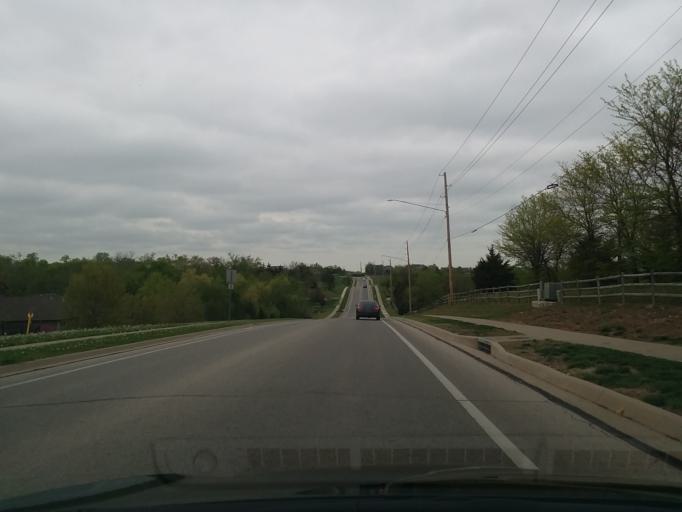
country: US
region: Kansas
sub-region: Douglas County
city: Lawrence
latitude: 38.9806
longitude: -95.2882
